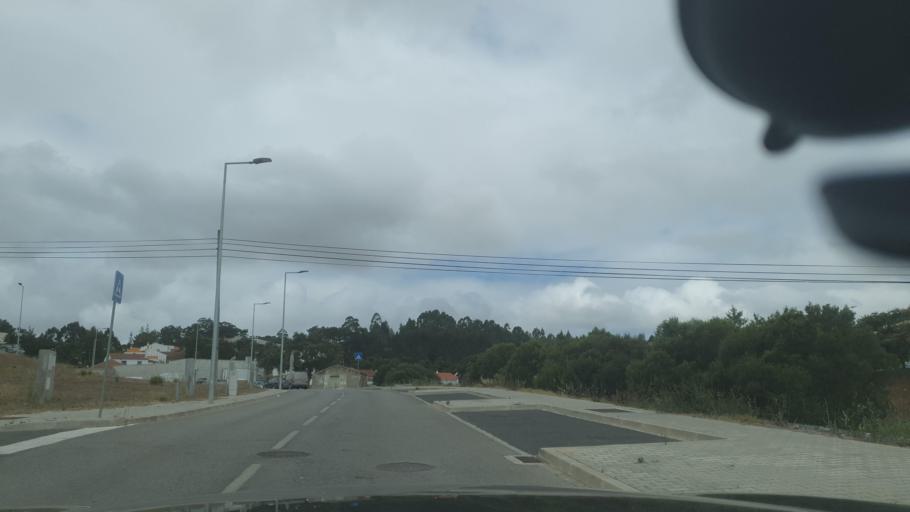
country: PT
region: Beja
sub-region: Odemira
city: Sao Teotonio
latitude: 37.5098
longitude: -8.7043
